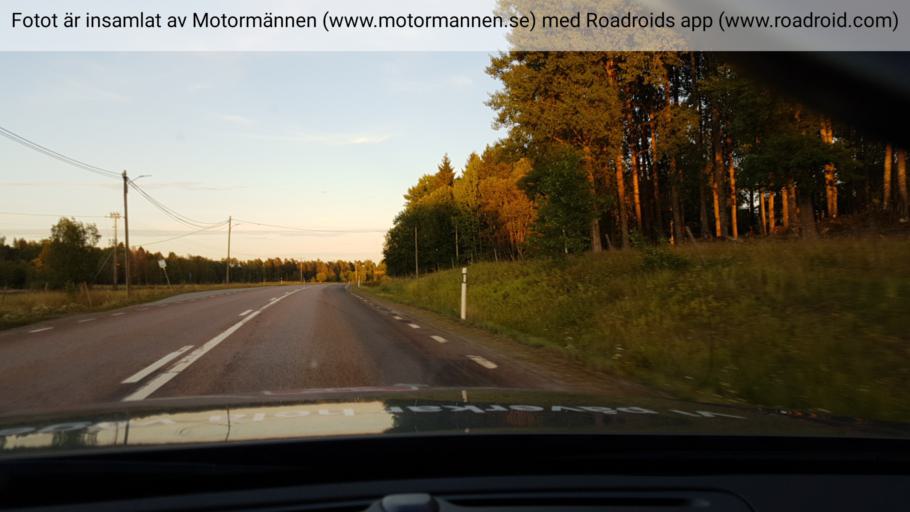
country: SE
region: OErebro
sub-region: Karlskoga Kommun
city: Karlskoga
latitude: 59.3928
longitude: 14.4583
